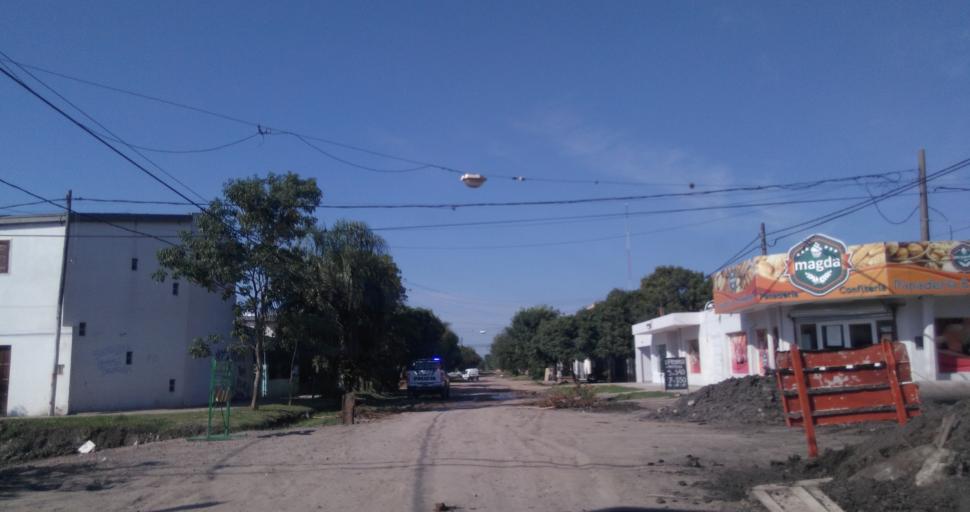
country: AR
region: Chaco
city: Resistencia
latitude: -27.4686
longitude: -58.9718
